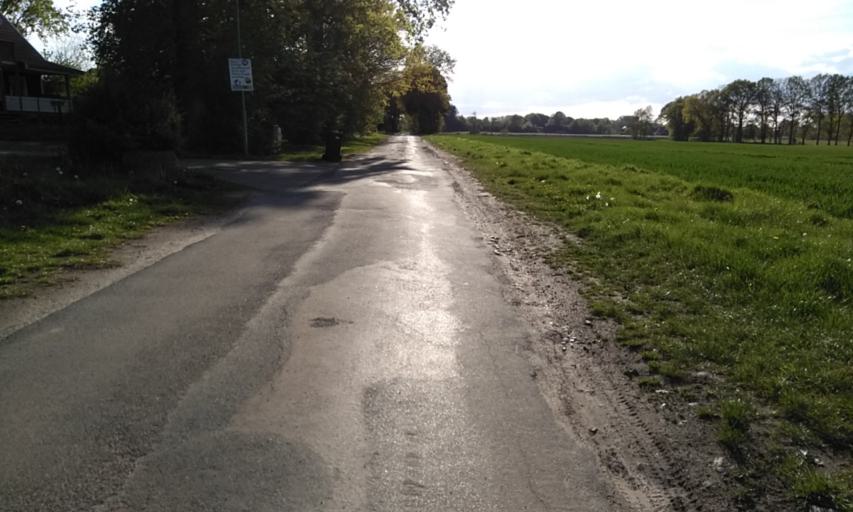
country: DE
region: Lower Saxony
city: Beckdorf
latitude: 53.4066
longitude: 9.6250
